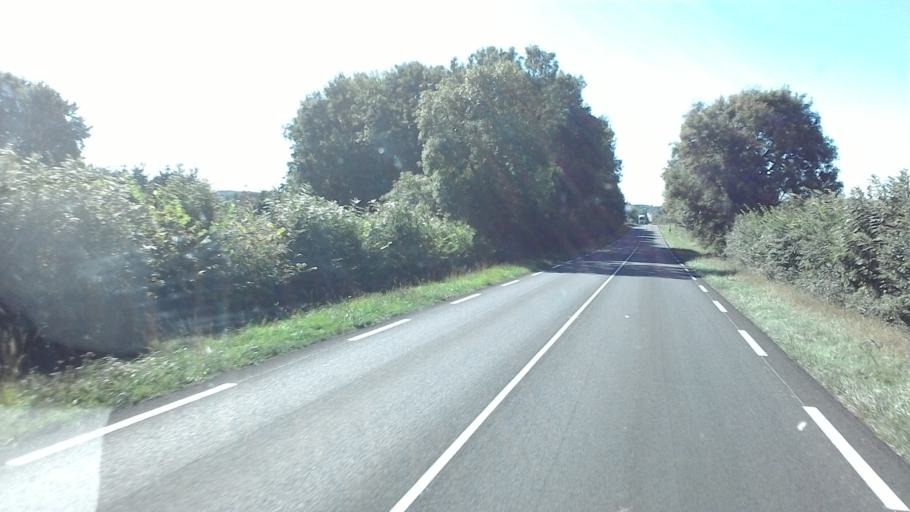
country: FR
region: Bourgogne
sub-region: Departement de la Cote-d'Or
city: Saulieu
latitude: 47.3670
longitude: 4.2890
